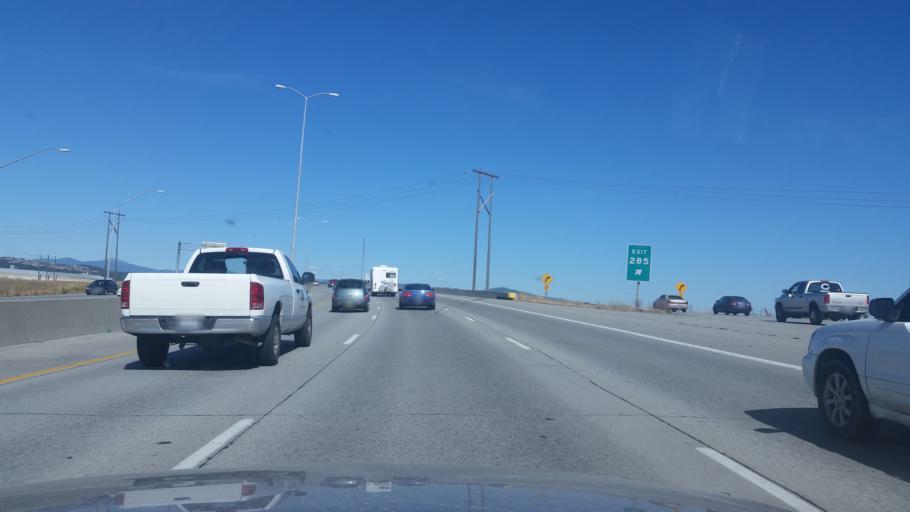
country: US
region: Washington
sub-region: Spokane County
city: Dishman
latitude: 47.6550
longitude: -117.3242
